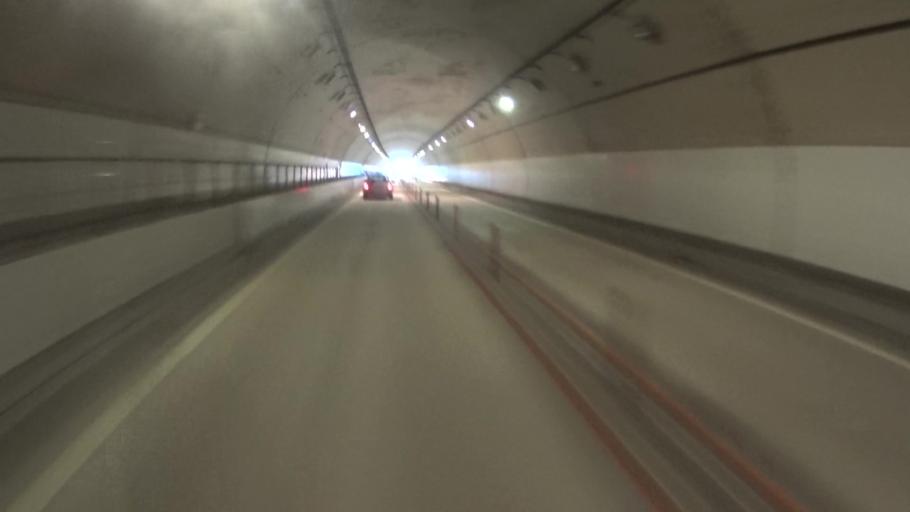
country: JP
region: Kyoto
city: Miyazu
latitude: 35.5215
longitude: 135.1834
